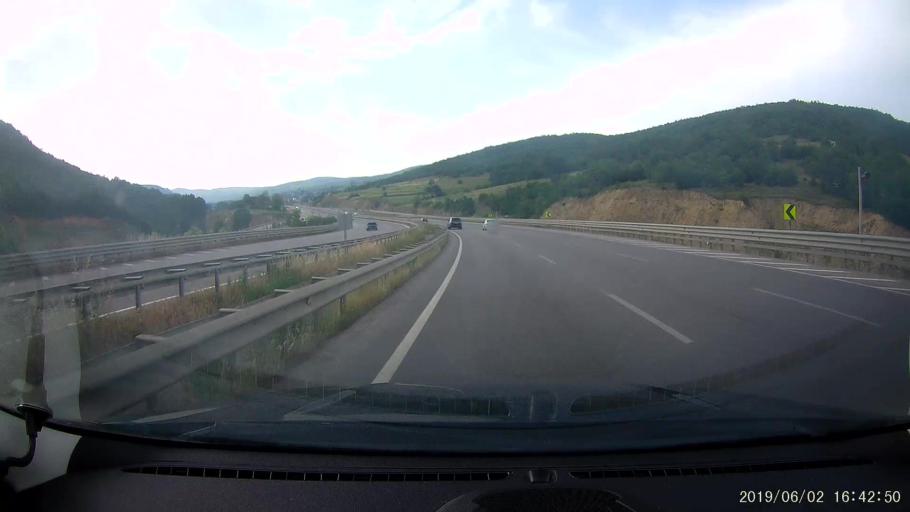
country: TR
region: Samsun
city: Kavak
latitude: 41.1247
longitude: 36.1379
